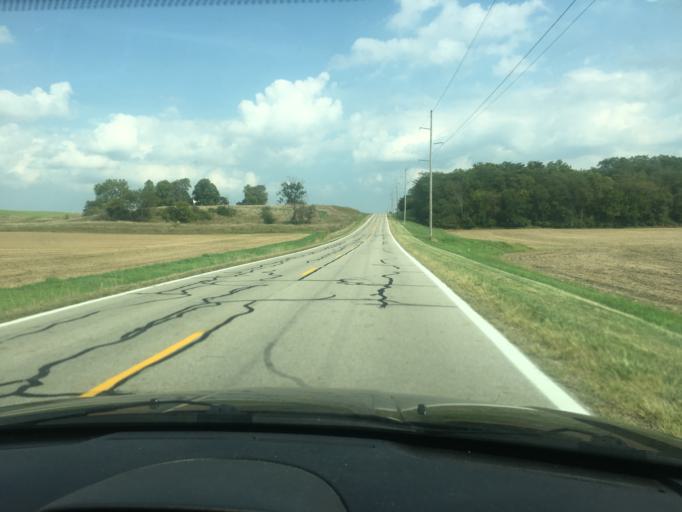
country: US
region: Ohio
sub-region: Champaign County
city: Urbana
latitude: 40.1285
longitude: -83.7875
